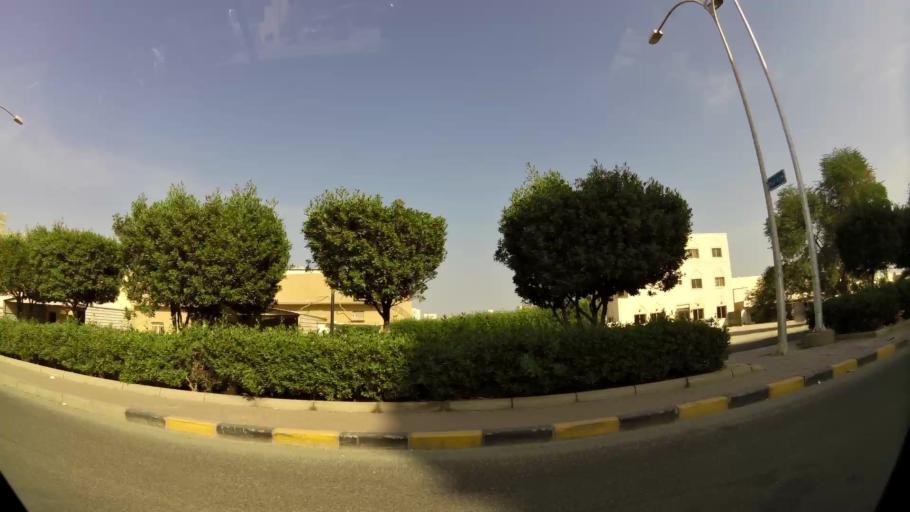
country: KW
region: Al Ahmadi
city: Ar Riqqah
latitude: 29.1371
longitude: 48.1087
